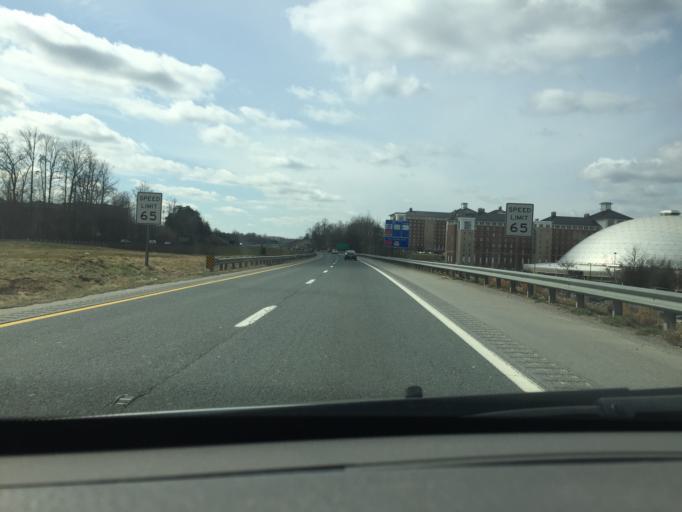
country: US
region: Virginia
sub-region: City of Lynchburg
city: West Lynchburg
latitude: 37.3499
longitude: -79.1779
